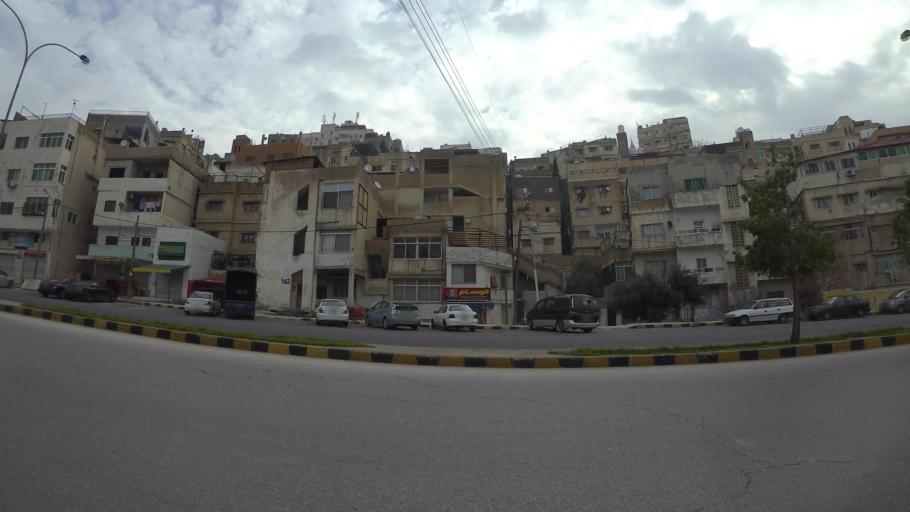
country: JO
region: Amman
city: Amman
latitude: 31.9640
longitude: 35.9345
